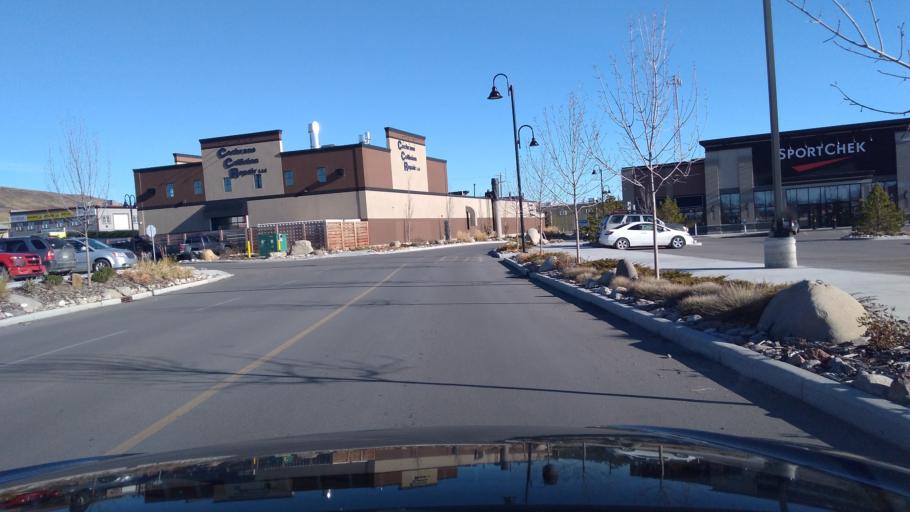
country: CA
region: Alberta
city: Cochrane
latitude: 51.1847
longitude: -114.4694
